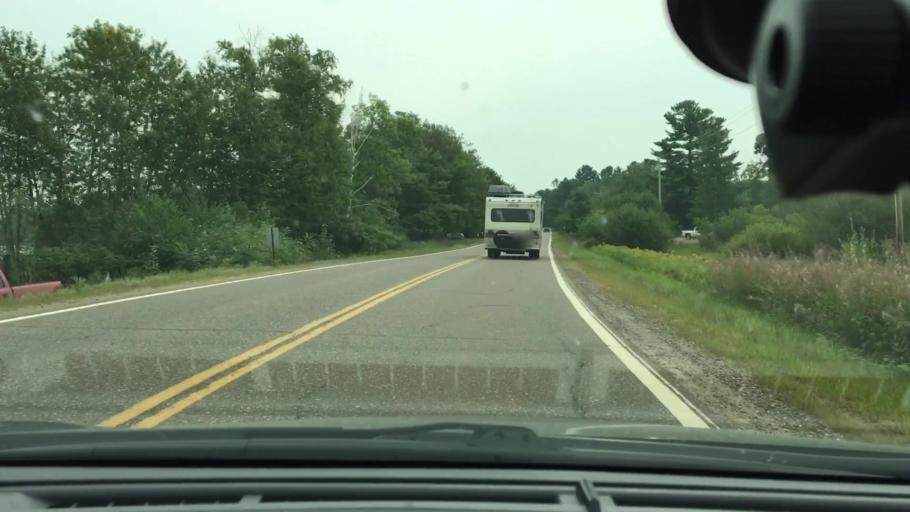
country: US
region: Minnesota
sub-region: Aitkin County
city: Aitkin
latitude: 46.4039
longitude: -93.7776
